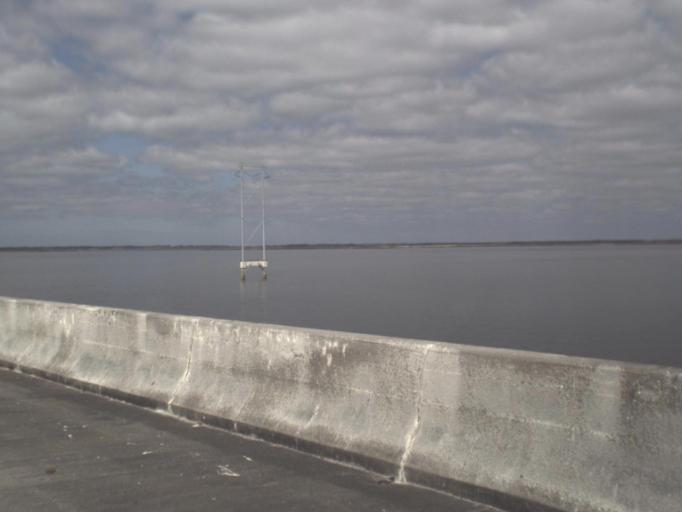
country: US
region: Florida
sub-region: Franklin County
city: Apalachicola
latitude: 29.7301
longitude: -84.9399
